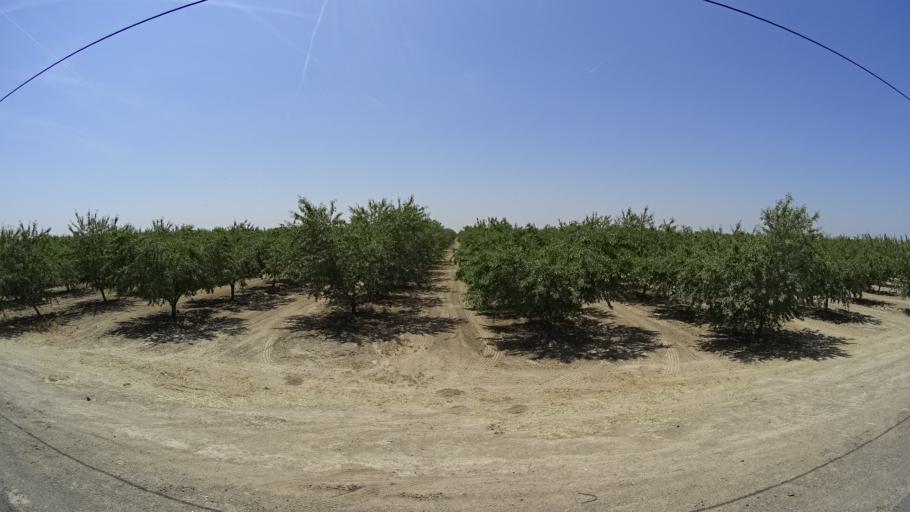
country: US
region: California
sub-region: Fresno County
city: Kingsburg
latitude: 36.4014
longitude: -119.5486
